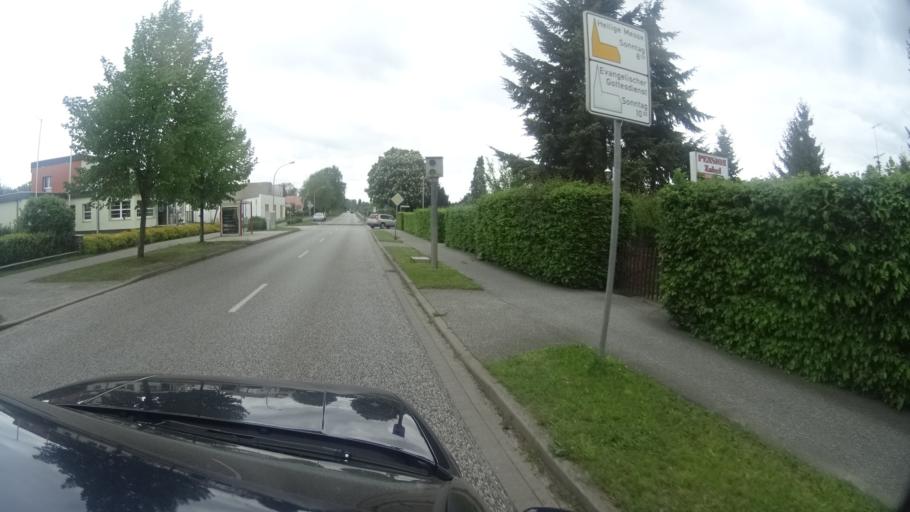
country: DE
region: Brandenburg
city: Fehrbellin
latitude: 52.8071
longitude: 12.7832
